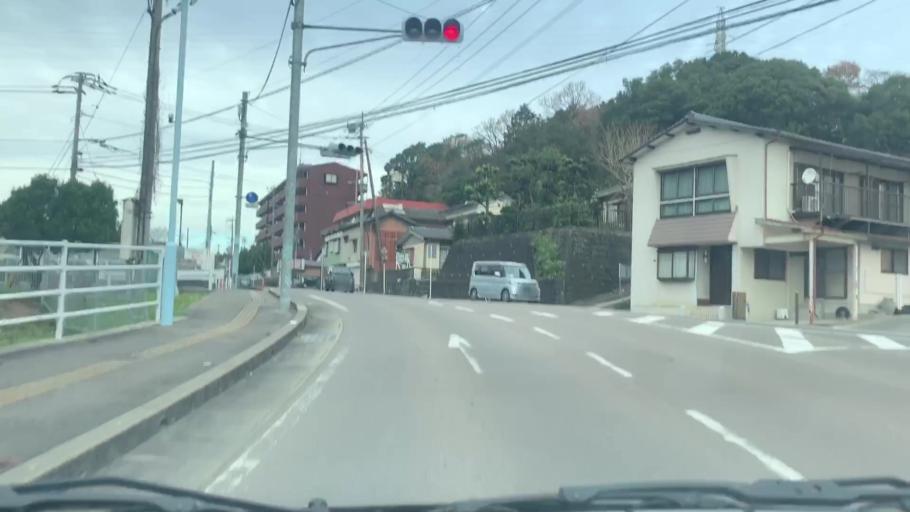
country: JP
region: Saga Prefecture
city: Ureshinomachi-shimojuku
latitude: 33.1000
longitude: 129.9797
